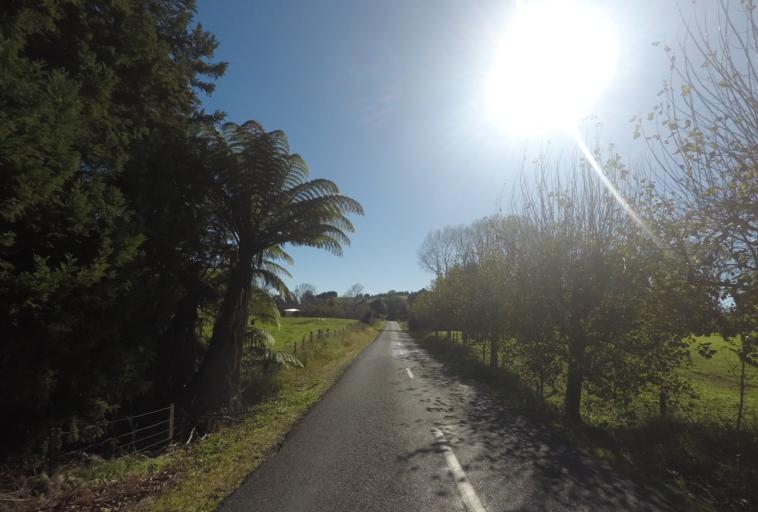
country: NZ
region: Bay of Plenty
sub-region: Western Bay of Plenty District
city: Waihi Beach
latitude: -37.4010
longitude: 175.9063
